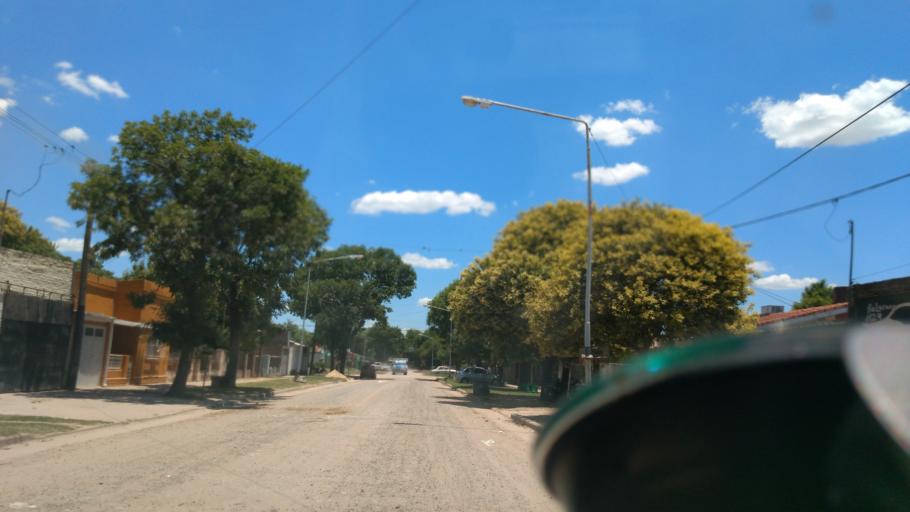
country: AR
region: Santa Fe
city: Laguna Paiva
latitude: -31.3117
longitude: -60.6599
